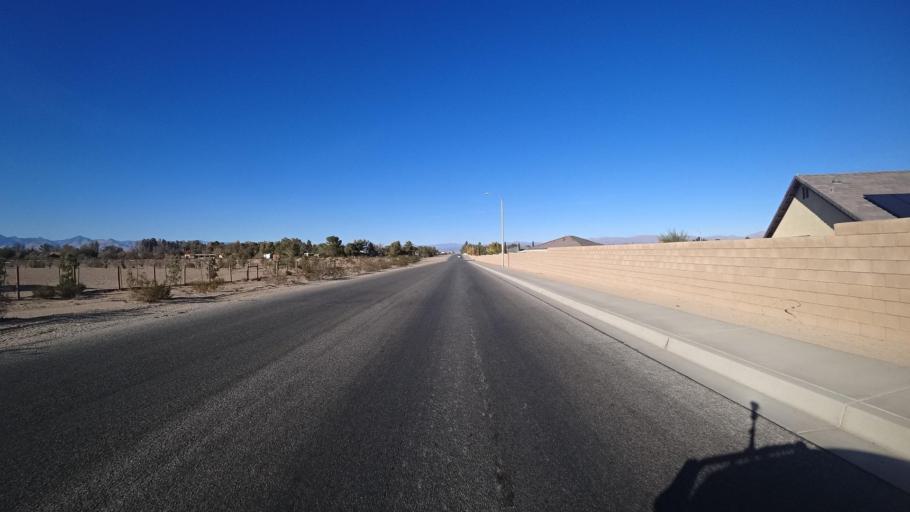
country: US
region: California
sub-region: Kern County
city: Ridgecrest
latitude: 35.6393
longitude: -117.6965
